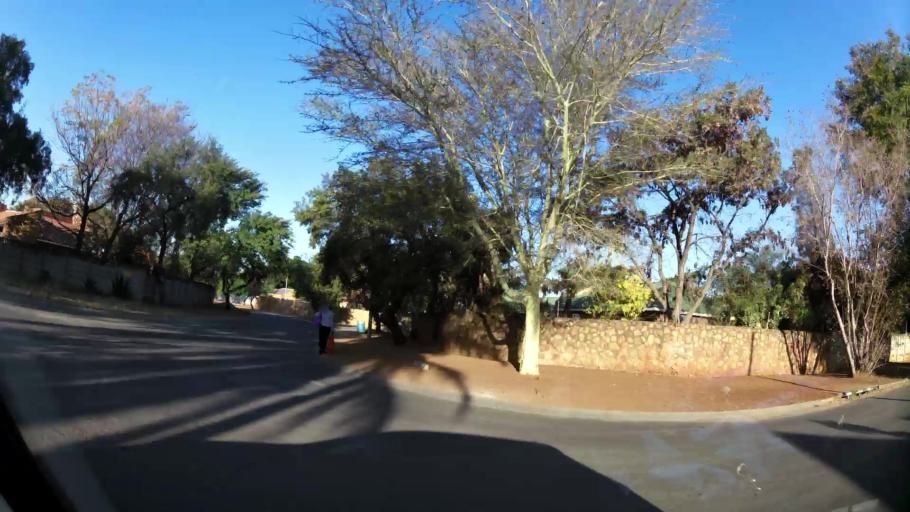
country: ZA
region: North-West
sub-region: Bojanala Platinum District Municipality
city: Rustenburg
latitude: -25.6746
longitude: 27.2055
